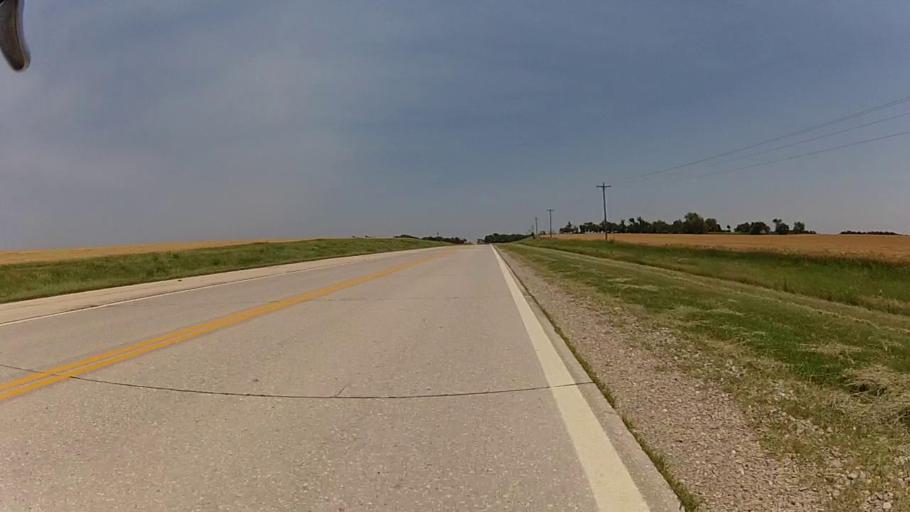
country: US
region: Kansas
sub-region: Cowley County
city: Arkansas City
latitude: 37.0571
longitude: -97.2424
